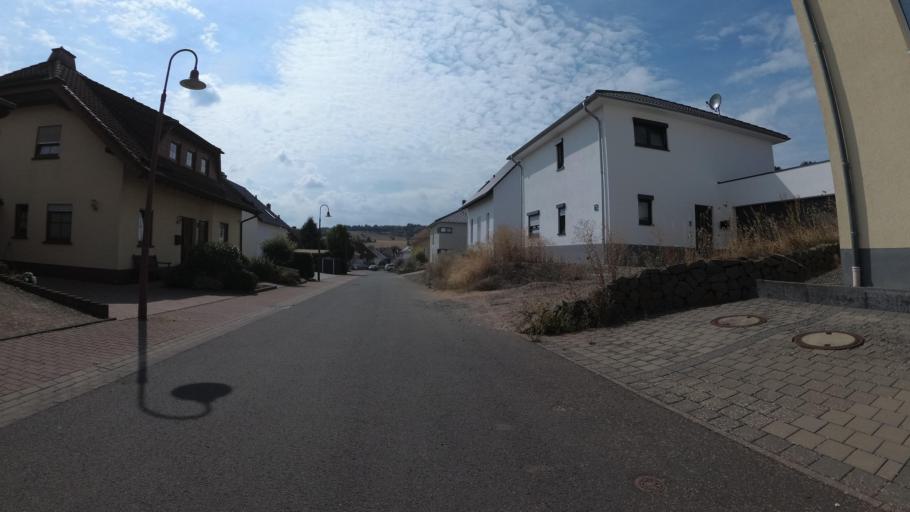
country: DE
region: Rheinland-Pfalz
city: Wahnwegen
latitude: 49.4867
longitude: 7.3808
